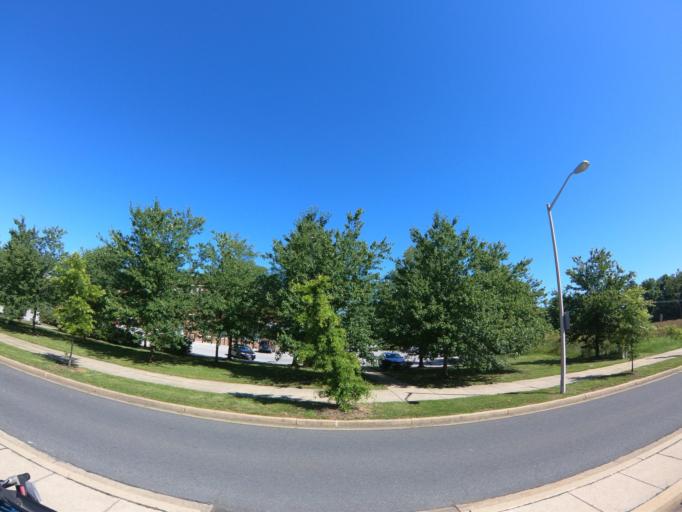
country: US
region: Maryland
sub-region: Prince George's County
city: Lake Arbor
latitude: 38.9034
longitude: -76.8351
